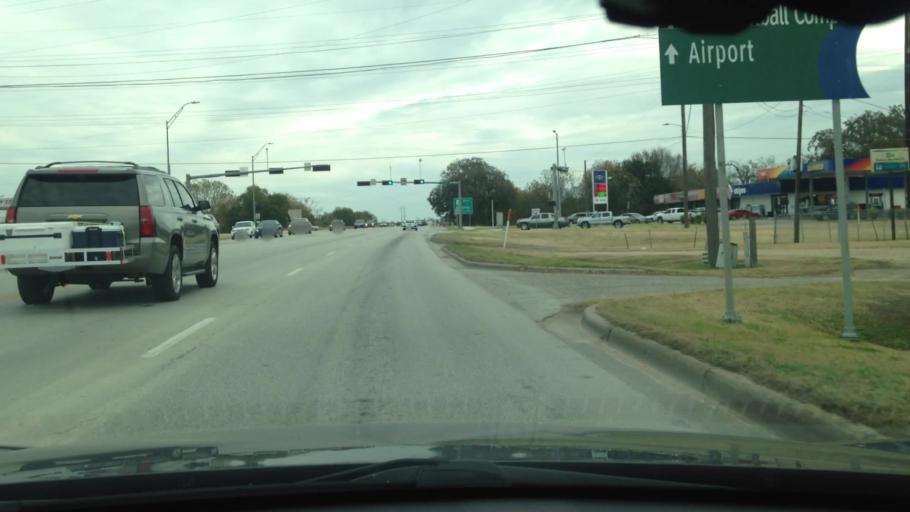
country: US
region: Texas
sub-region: Hays County
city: San Marcos
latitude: 29.8810
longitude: -97.9141
